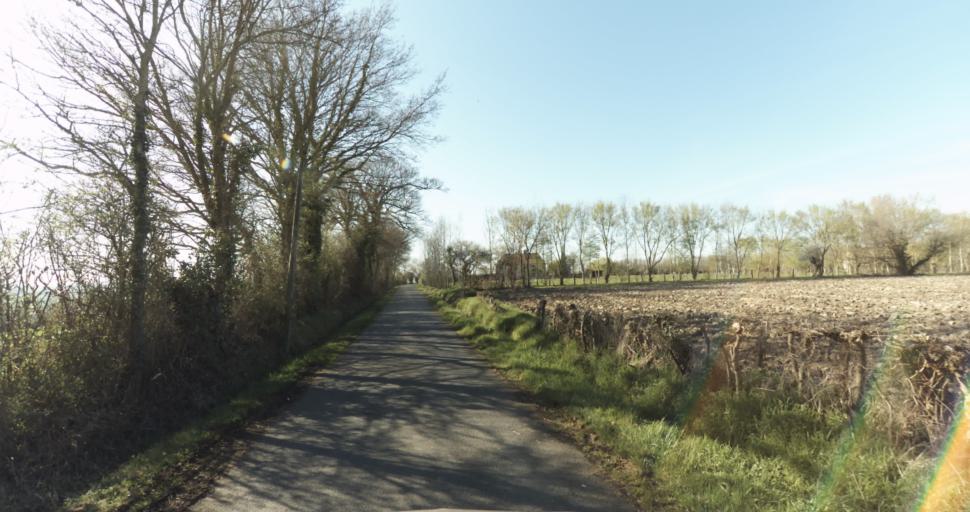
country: FR
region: Lower Normandy
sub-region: Departement du Calvados
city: Saint-Pierre-sur-Dives
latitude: 49.0454
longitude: 0.0338
